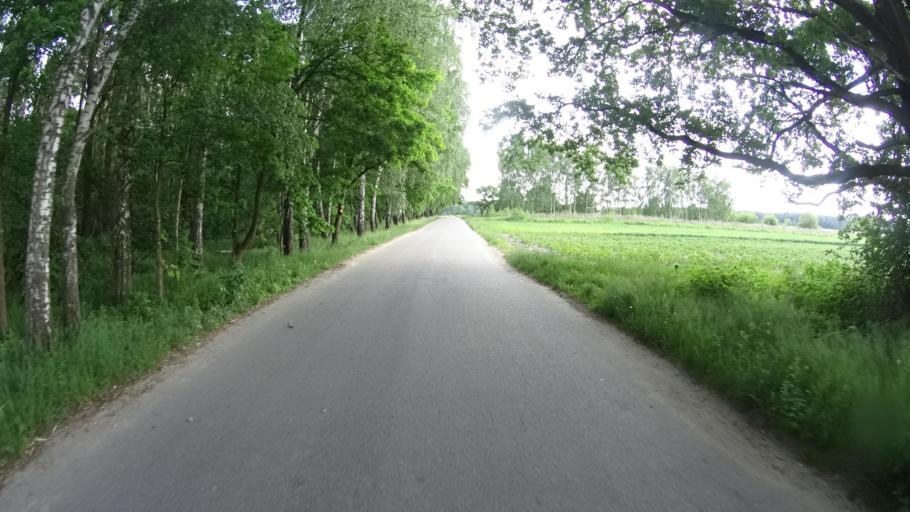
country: PL
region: Masovian Voivodeship
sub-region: Warszawa
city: Kabaty
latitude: 52.1139
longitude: 21.0856
